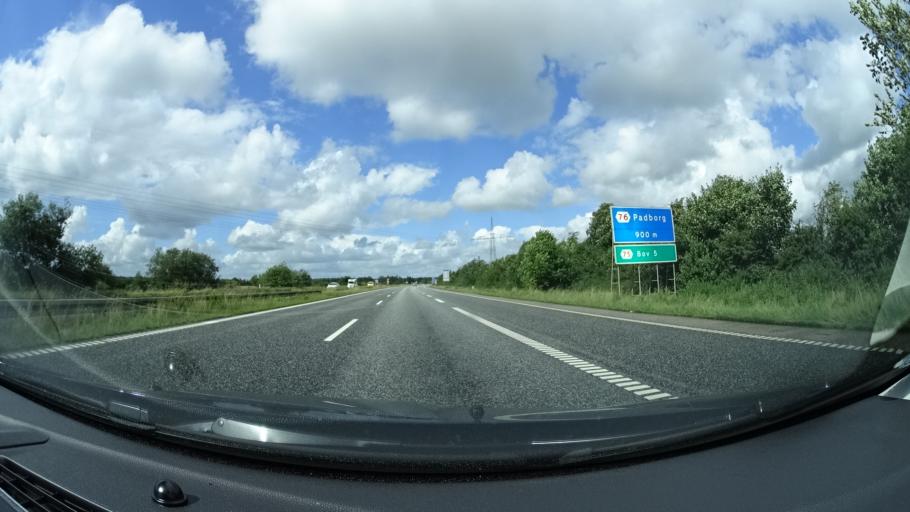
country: DK
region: South Denmark
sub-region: Aabenraa Kommune
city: Padborg
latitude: 54.8092
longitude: 9.3267
